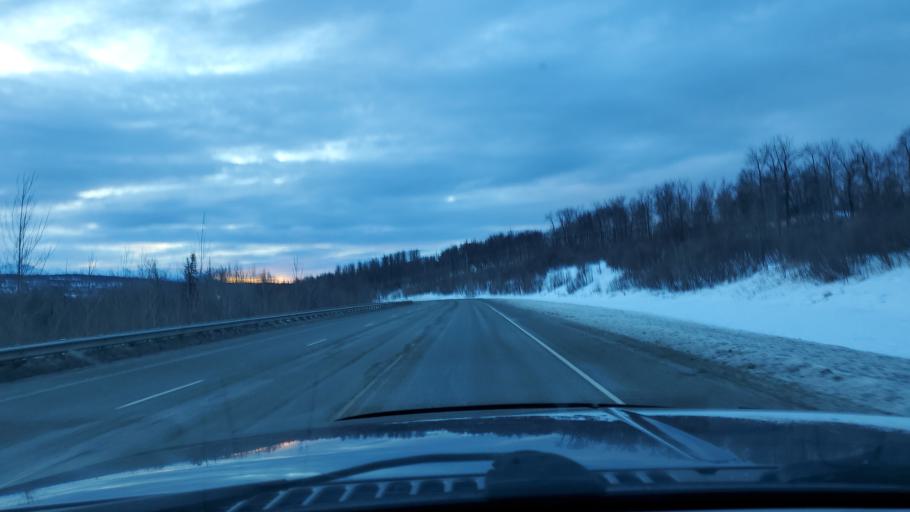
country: US
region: Alaska
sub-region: Matanuska-Susitna Borough
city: Lazy Mountain
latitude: 61.6889
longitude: -148.9788
